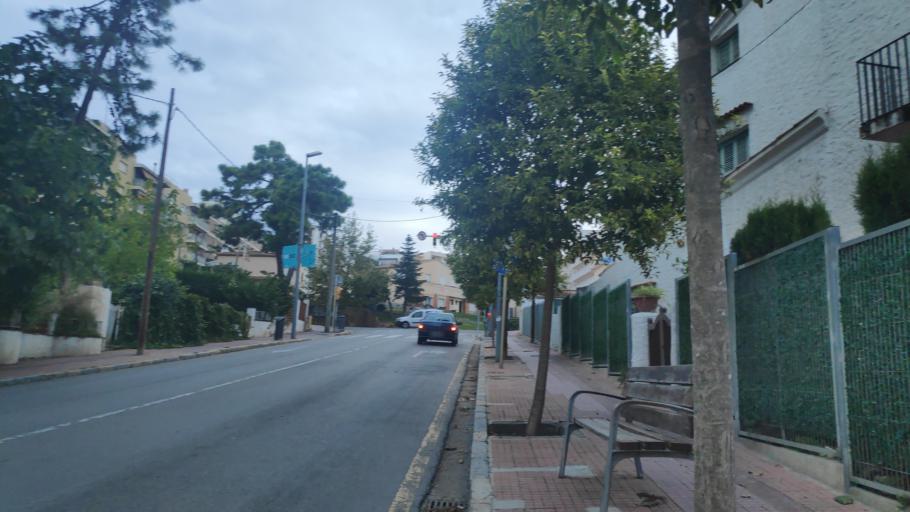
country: ES
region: Catalonia
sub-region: Provincia de Girona
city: Lloret de Mar
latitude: 41.7033
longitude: 2.8551
